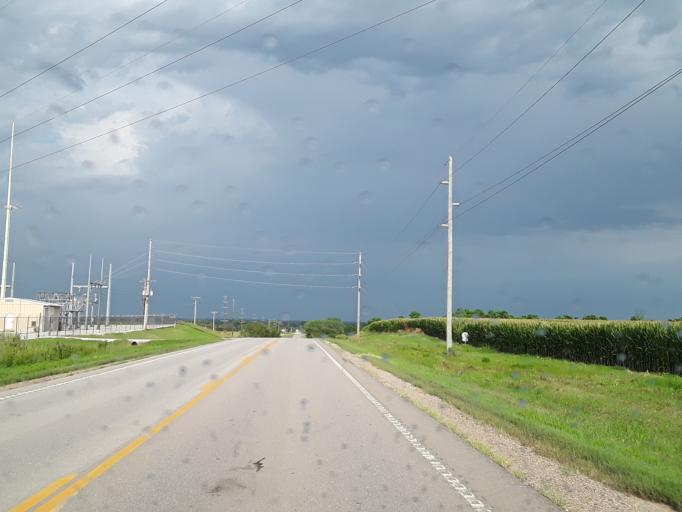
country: US
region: Nebraska
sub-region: Saunders County
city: Ashland
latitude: 41.0887
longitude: -96.3865
